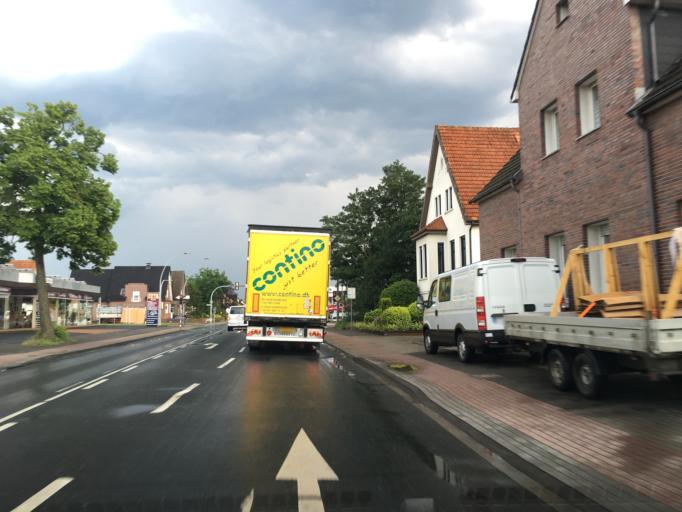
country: DE
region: North Rhine-Westphalia
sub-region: Regierungsbezirk Munster
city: Steinfurt
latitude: 52.1145
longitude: 7.3985
